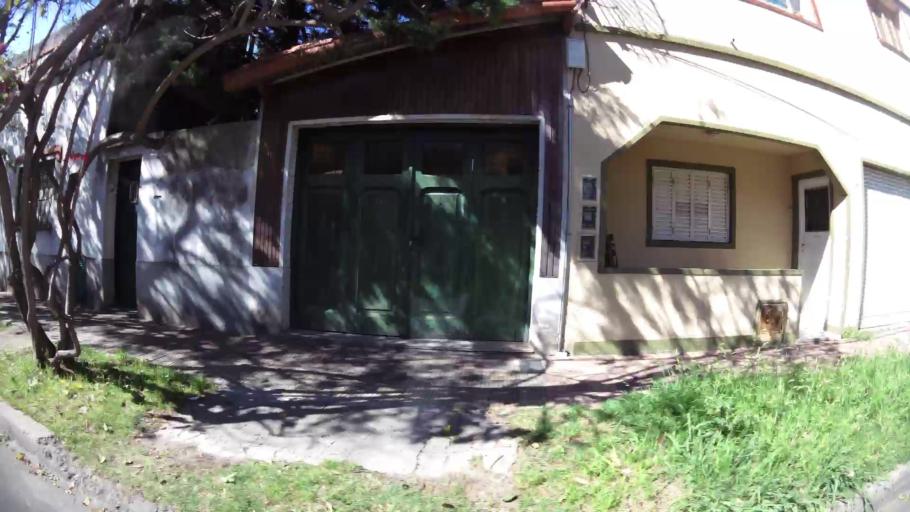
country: AR
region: Buenos Aires
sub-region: Partido de General San Martin
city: General San Martin
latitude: -34.5443
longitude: -58.5087
